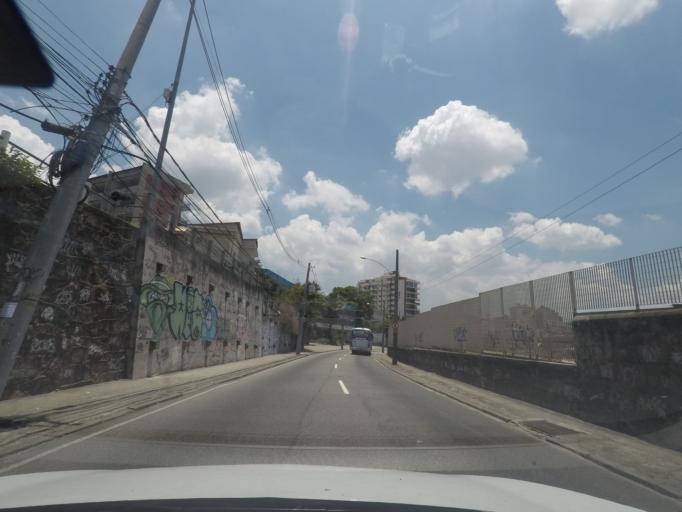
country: BR
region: Rio de Janeiro
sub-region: Rio De Janeiro
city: Rio de Janeiro
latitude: -22.9047
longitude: -43.2733
